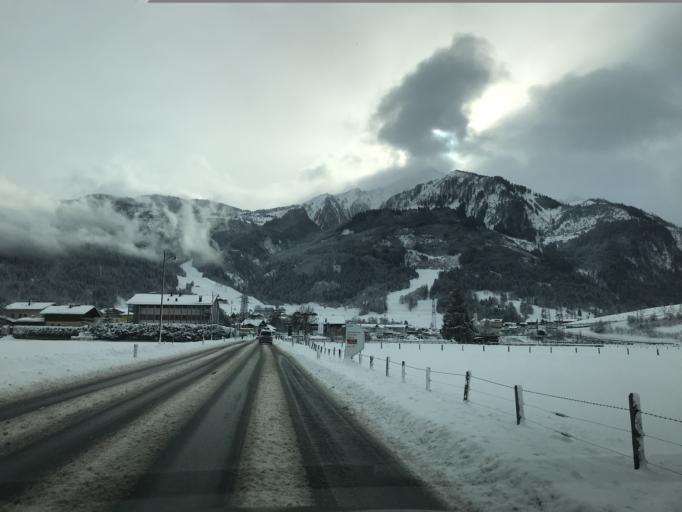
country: AT
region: Salzburg
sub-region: Politischer Bezirk Zell am See
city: Kaprun
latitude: 47.2802
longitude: 12.7555
